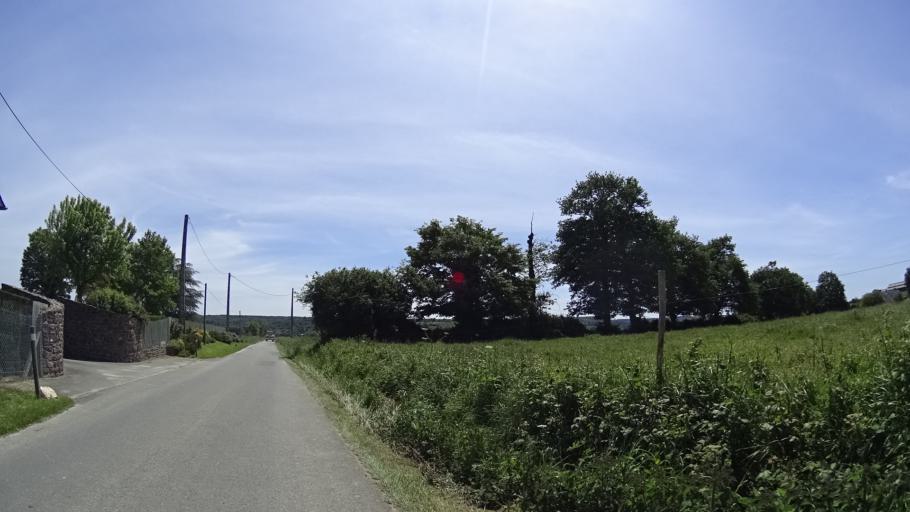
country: FR
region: Brittany
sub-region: Departement d'Ille-et-Vilaine
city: Iffendic
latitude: 48.1431
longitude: -1.9968
